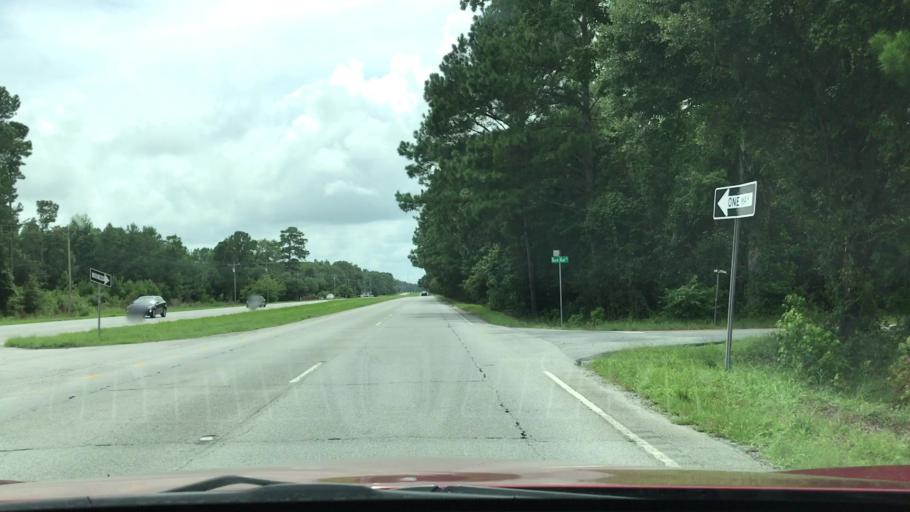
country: US
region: South Carolina
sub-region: Charleston County
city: Awendaw
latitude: 33.0542
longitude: -79.5490
